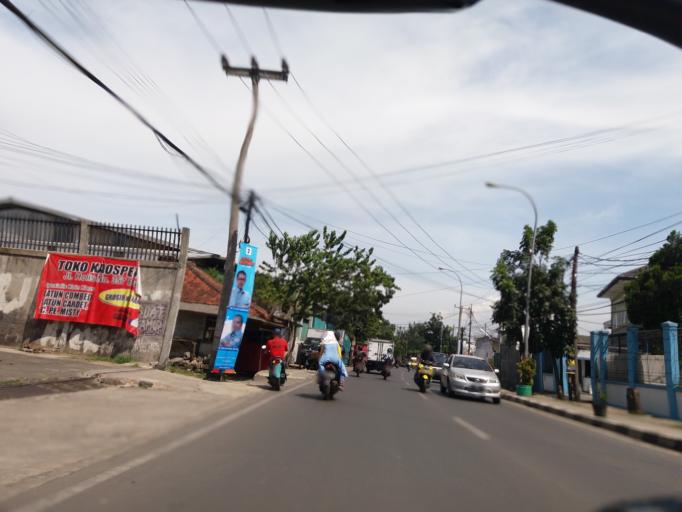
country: ID
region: West Java
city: Margahayukencana
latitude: -6.9411
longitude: 107.5679
